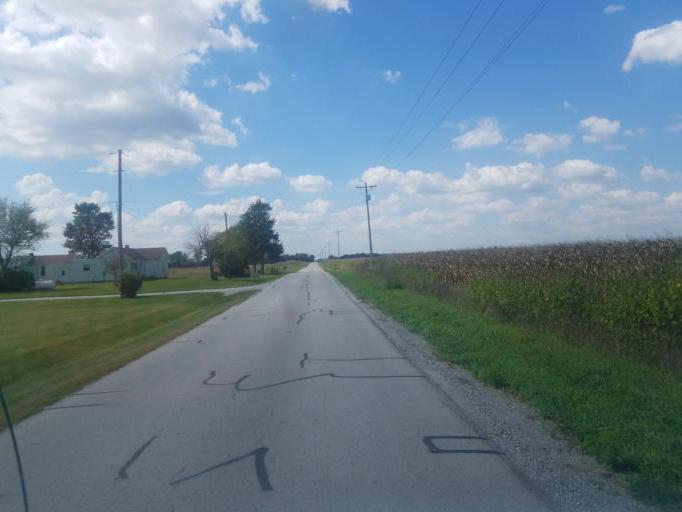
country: US
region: Ohio
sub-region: Hardin County
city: Ada
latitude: 40.6519
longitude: -83.9267
